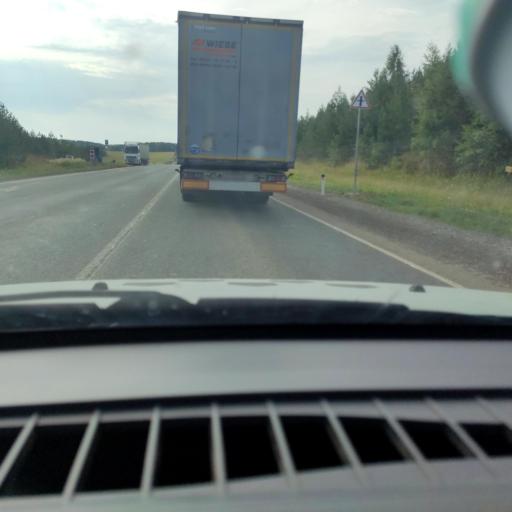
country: RU
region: Perm
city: Siva
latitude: 58.4170
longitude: 54.4630
